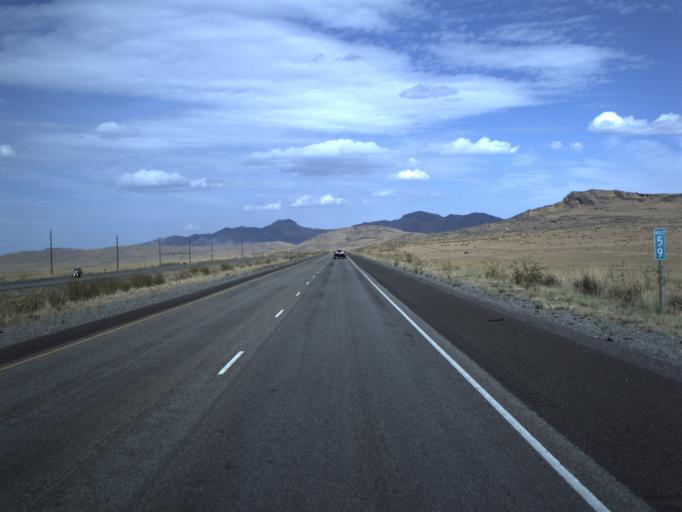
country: US
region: Utah
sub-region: Tooele County
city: Grantsville
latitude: 40.7971
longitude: -112.9467
